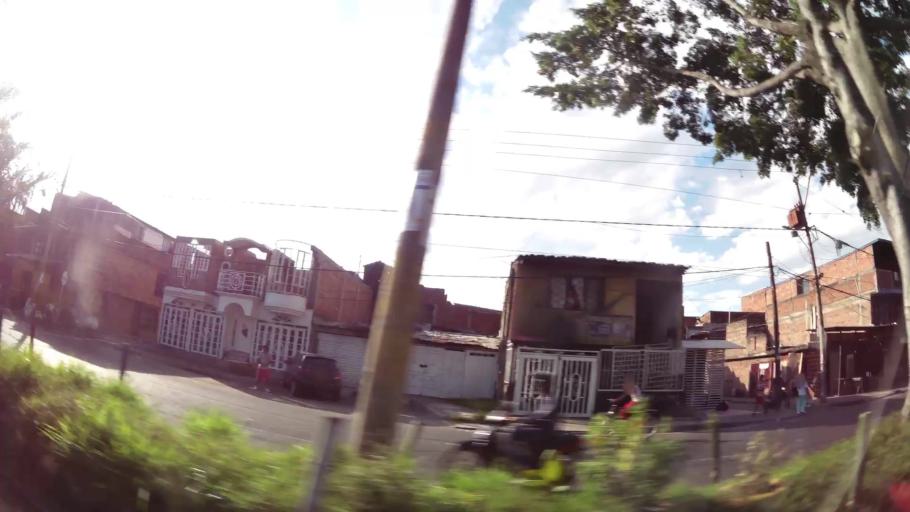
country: CO
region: Valle del Cauca
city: Cali
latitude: 3.4073
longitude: -76.4979
